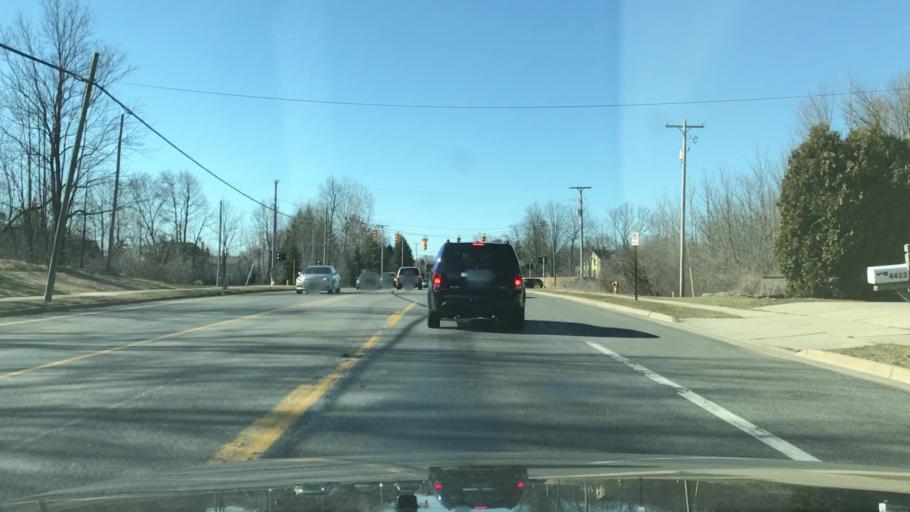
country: US
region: Michigan
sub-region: Kent County
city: East Grand Rapids
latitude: 42.9207
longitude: -85.5580
